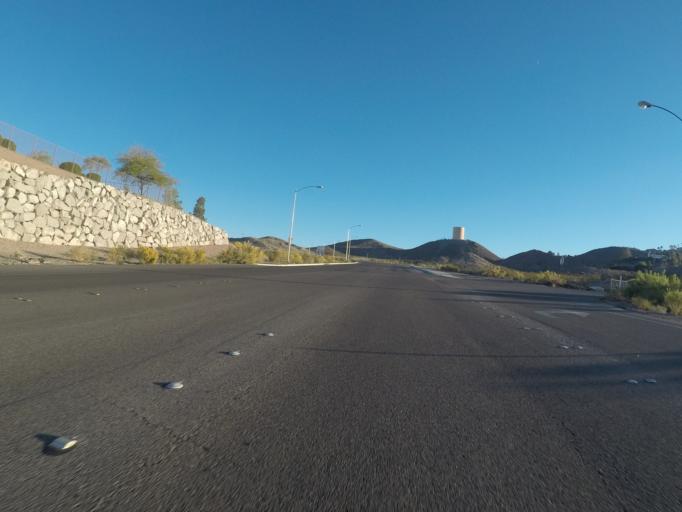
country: US
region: Nevada
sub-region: Clark County
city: Boulder City
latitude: 35.9874
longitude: -114.8307
